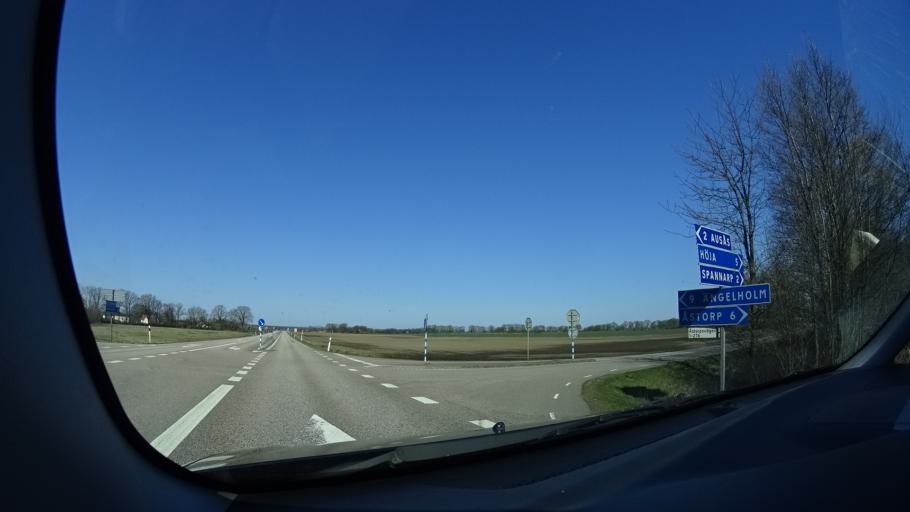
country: SE
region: Skane
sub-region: Angelholms Kommun
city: AEngelholm
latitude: 56.1830
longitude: 12.8918
